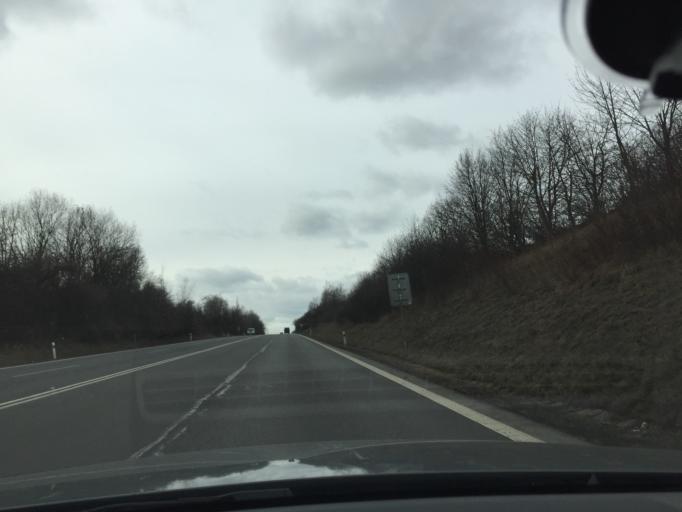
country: CZ
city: Frycovice
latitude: 49.6494
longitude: 18.2107
